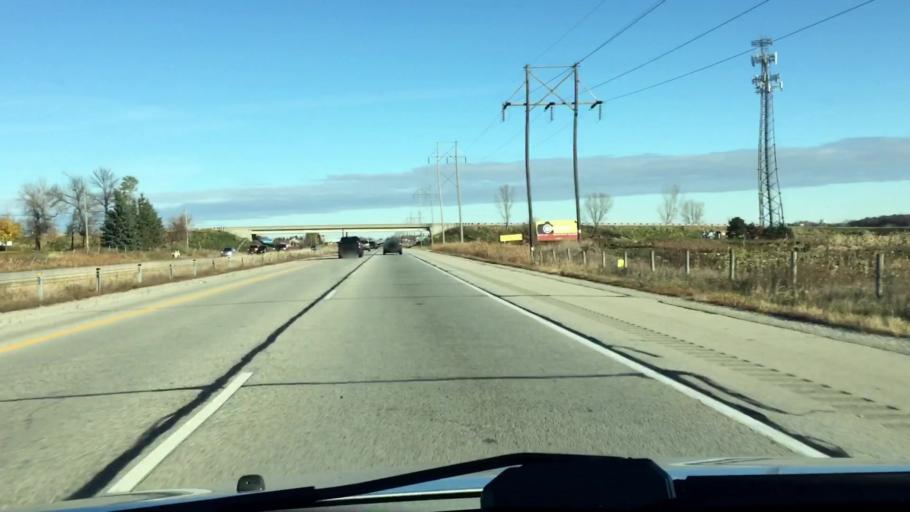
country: US
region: Wisconsin
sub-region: Winnebago County
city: Oshkosh
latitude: 43.9066
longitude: -88.5835
